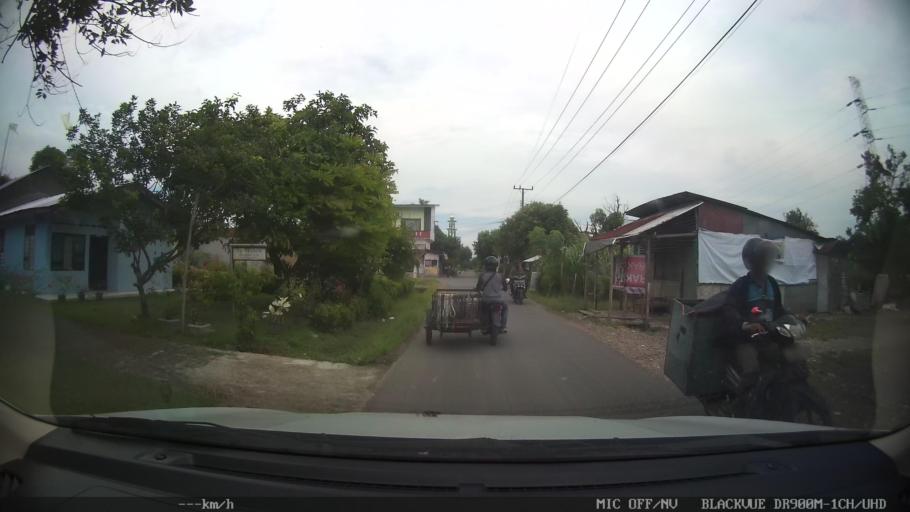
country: ID
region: North Sumatra
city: Sunggal
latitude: 3.6220
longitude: 98.5904
